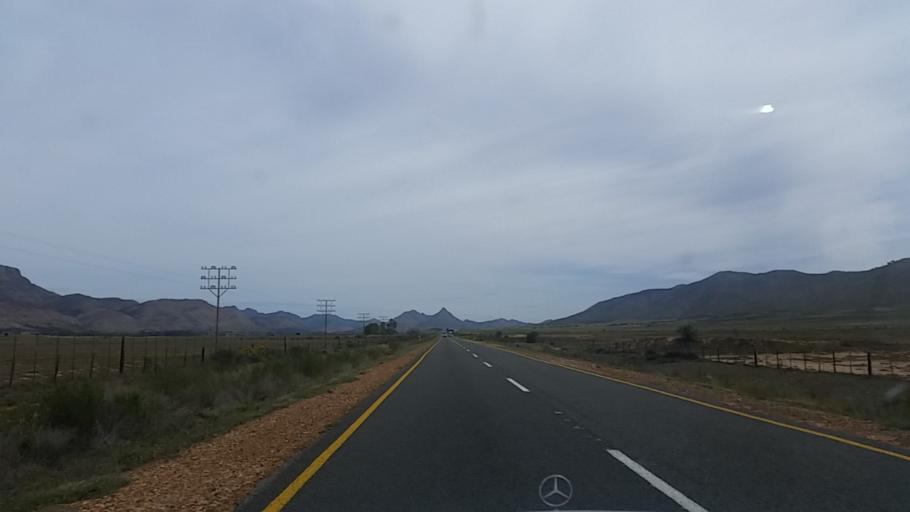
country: ZA
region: Western Cape
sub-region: Eden District Municipality
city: George
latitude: -33.8083
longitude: 22.5517
